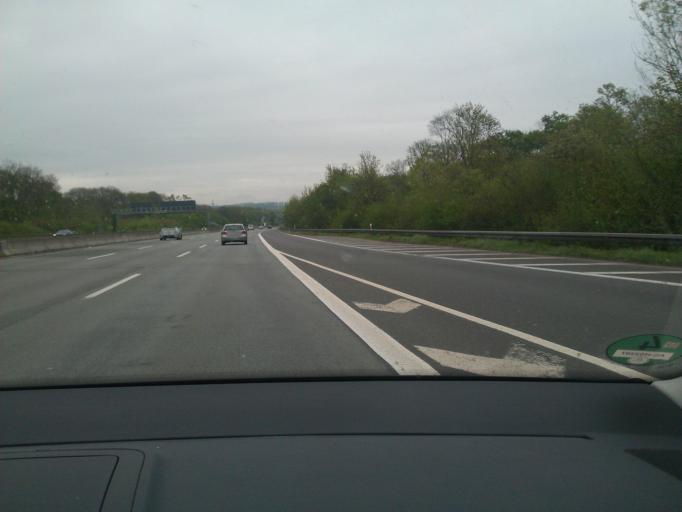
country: DE
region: North Rhine-Westphalia
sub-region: Regierungsbezirk Koln
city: Kerpen
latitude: 50.8974
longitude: 6.7009
